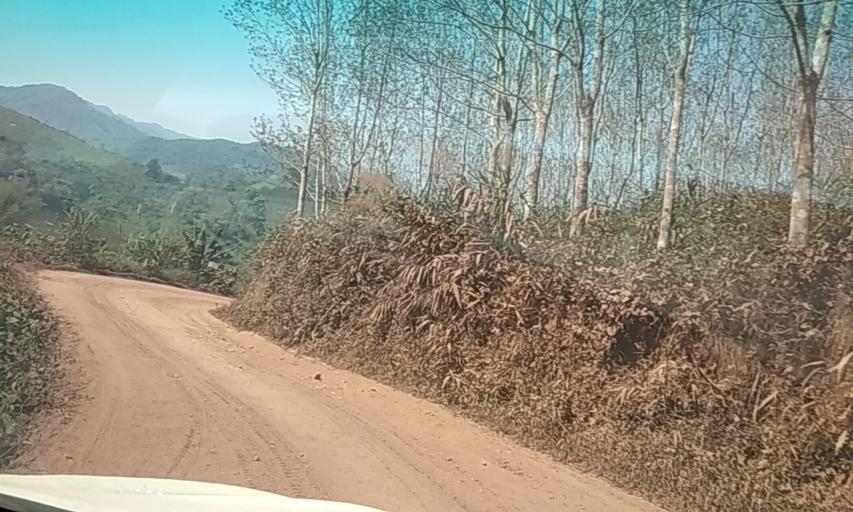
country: CN
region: Yunnan
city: Mengla
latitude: 21.5247
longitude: 101.8404
